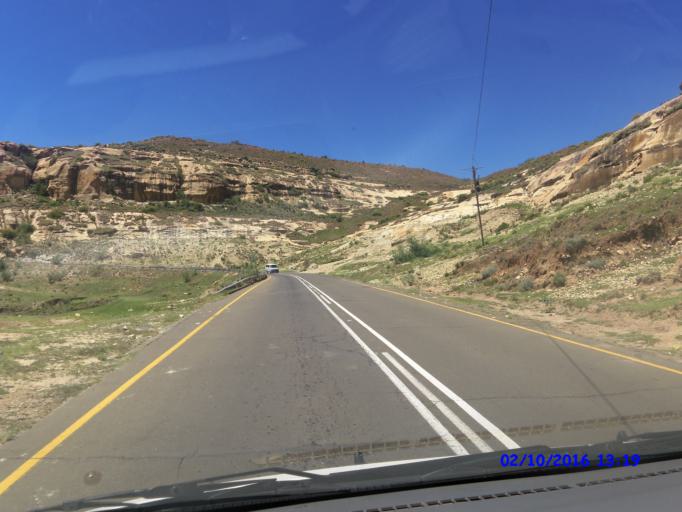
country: LS
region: Maseru
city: Nako
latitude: -29.4237
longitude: 27.6965
